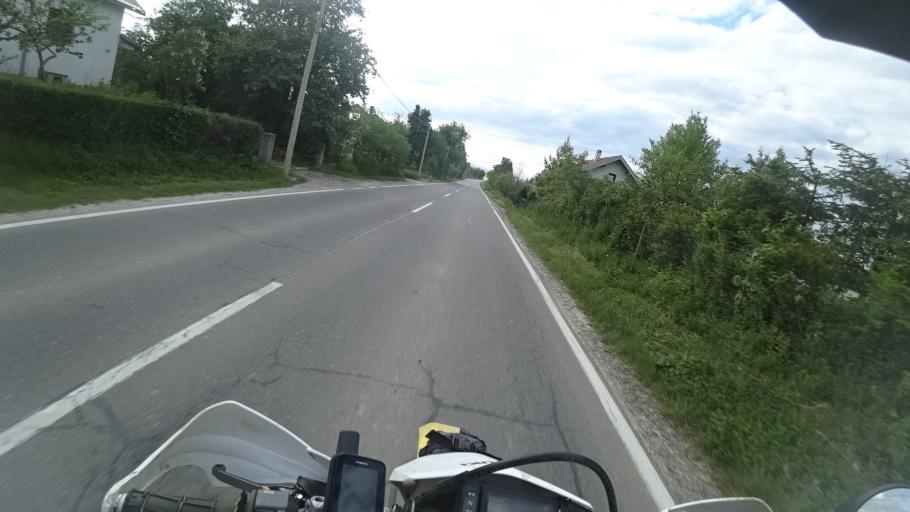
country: HR
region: Licko-Senjska
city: Gospic
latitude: 44.5310
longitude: 15.4016
